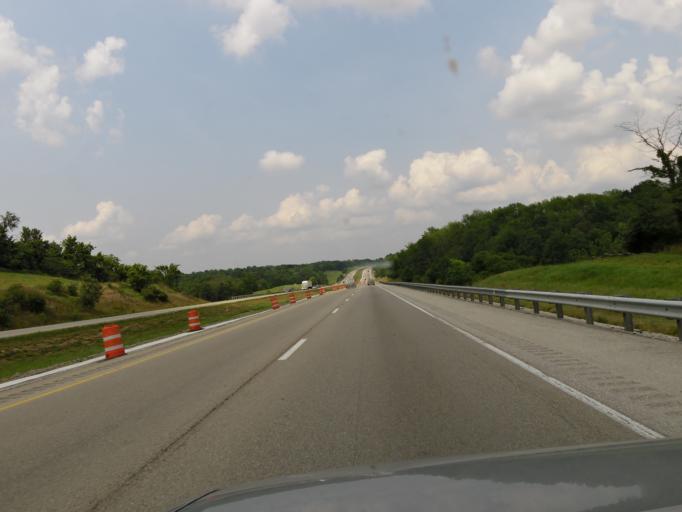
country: US
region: Kentucky
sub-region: Boone County
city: Verona
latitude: 38.8175
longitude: -84.7034
